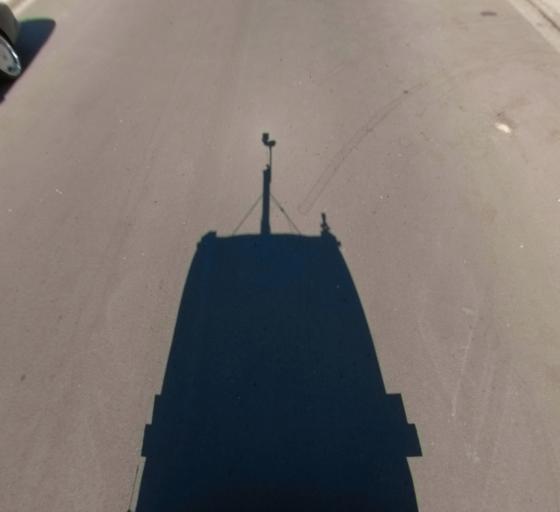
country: US
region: California
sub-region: Madera County
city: Parkwood
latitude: 36.9334
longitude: -120.0534
